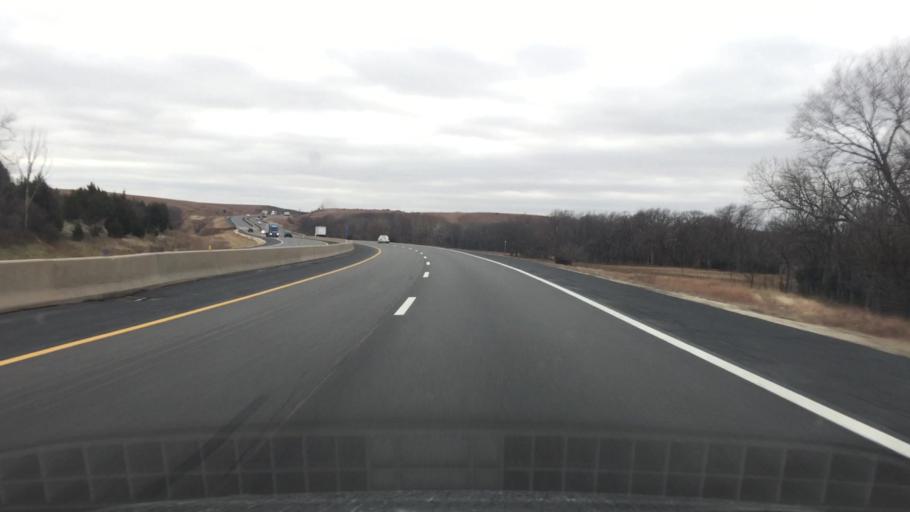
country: US
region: Kansas
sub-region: Chase County
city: Cottonwood Falls
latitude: 38.1420
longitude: -96.5231
